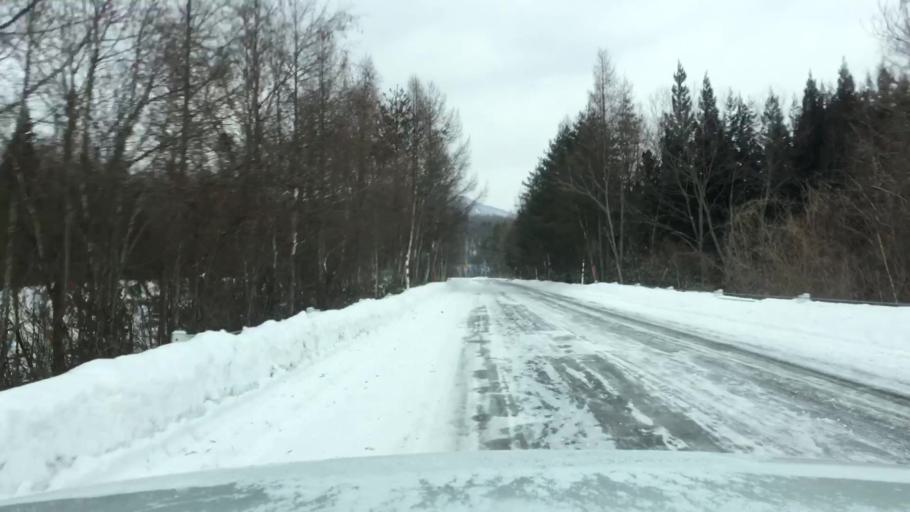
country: JP
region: Iwate
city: Shizukuishi
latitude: 39.9371
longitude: 141.0016
